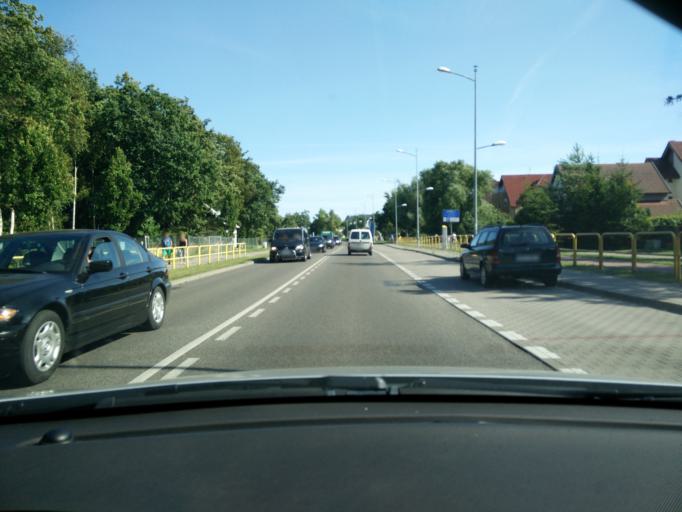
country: PL
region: Pomeranian Voivodeship
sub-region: Powiat pucki
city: Jastarnia
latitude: 54.7054
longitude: 18.6589
